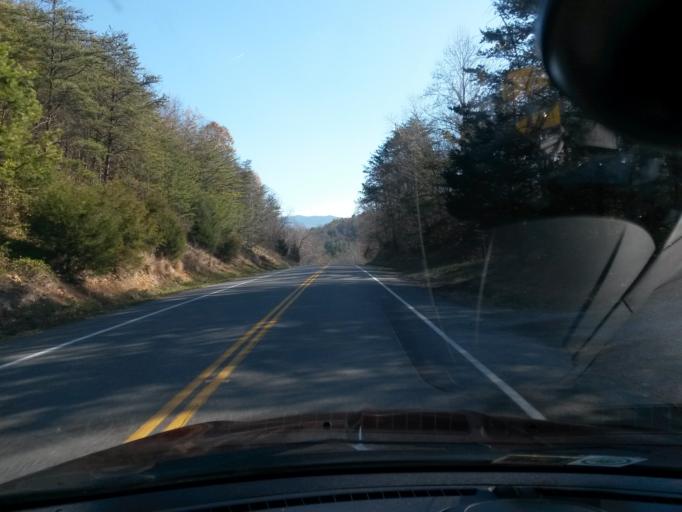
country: US
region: Virginia
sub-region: Botetourt County
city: Buchanan
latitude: 37.6413
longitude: -79.7895
